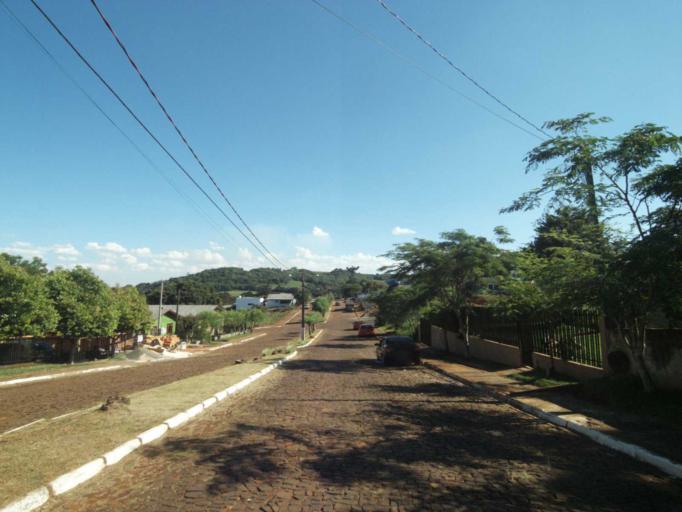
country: BR
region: Parana
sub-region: Laranjeiras Do Sul
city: Laranjeiras do Sul
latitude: -25.3822
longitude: -52.2034
